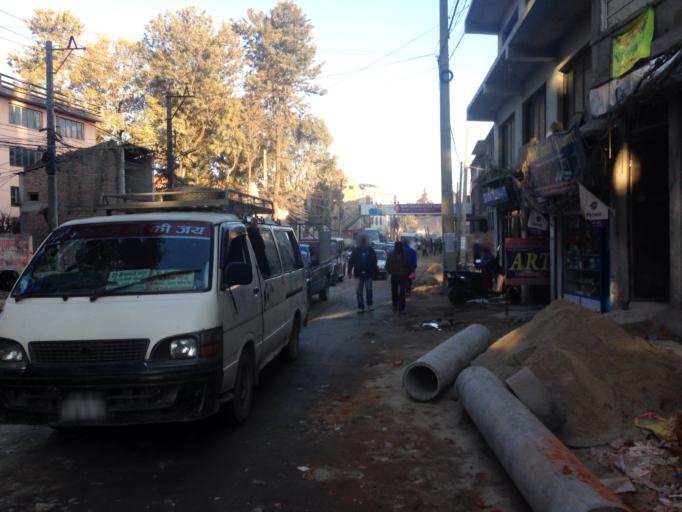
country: NP
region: Central Region
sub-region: Bagmati Zone
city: Kathmandu
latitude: 27.7182
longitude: 85.3122
